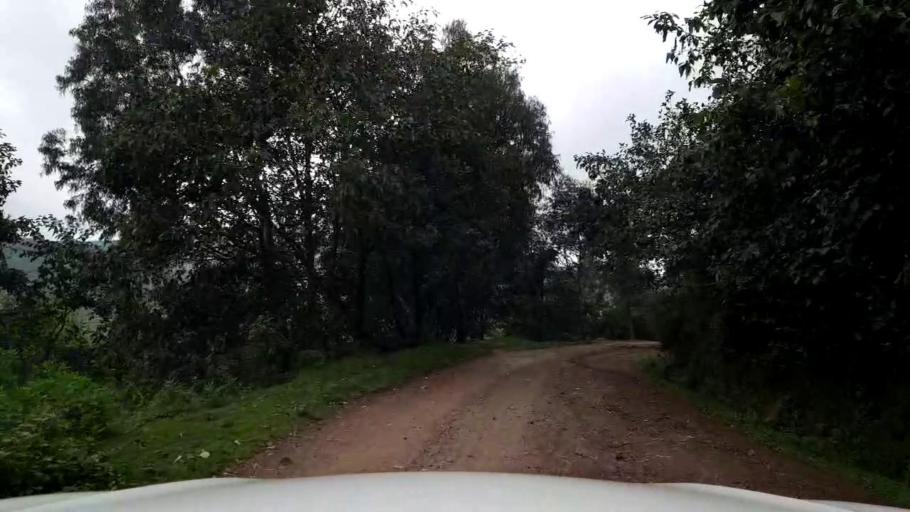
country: RW
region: Western Province
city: Gisenyi
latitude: -1.6571
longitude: 29.4186
